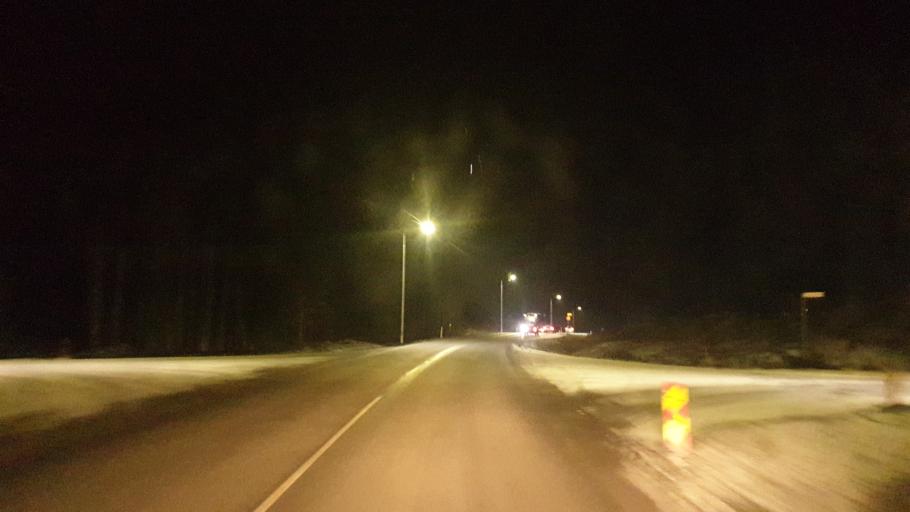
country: FI
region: Southern Savonia
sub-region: Pieksaemaeki
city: Juva
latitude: 61.8581
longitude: 27.7173
